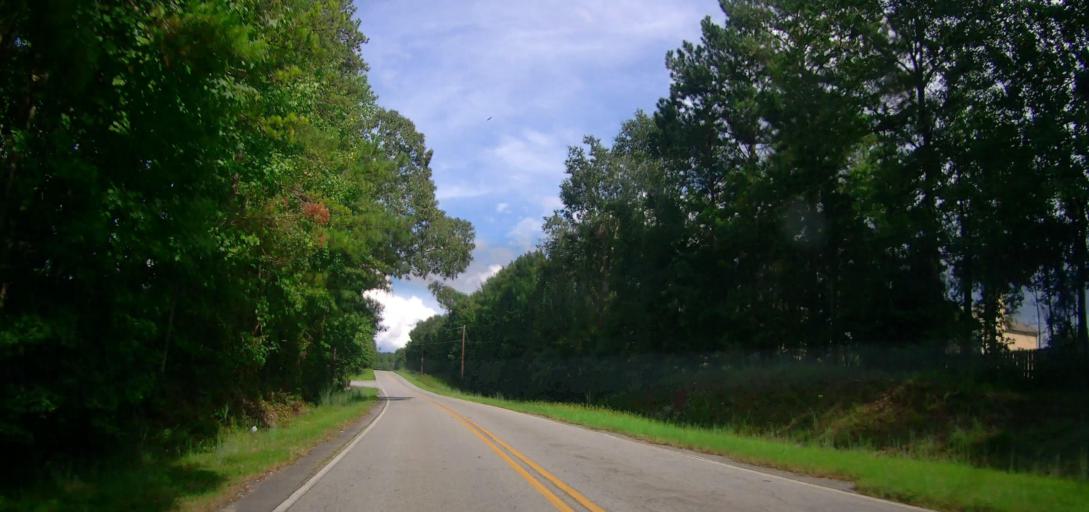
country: US
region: Alabama
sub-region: Russell County
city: Phenix City
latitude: 32.5894
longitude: -84.9189
